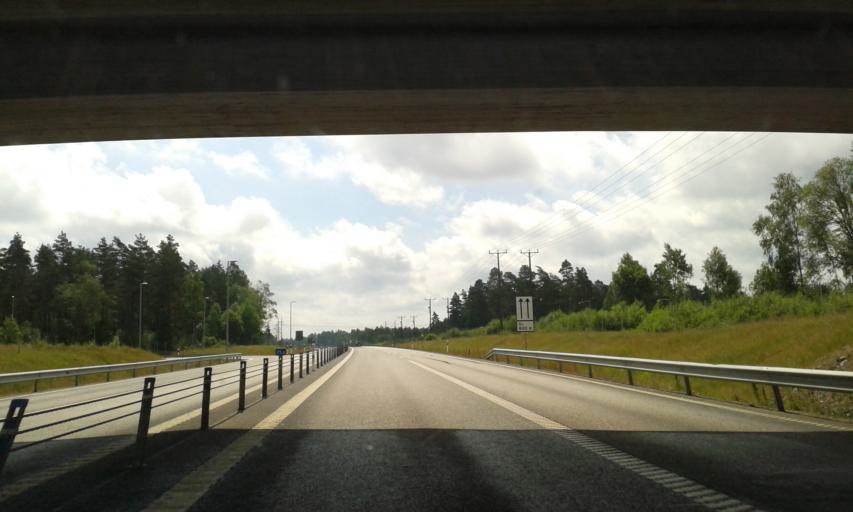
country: SE
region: Joenkoeping
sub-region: Gislaveds Kommun
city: Gislaved
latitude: 57.3007
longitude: 13.5834
